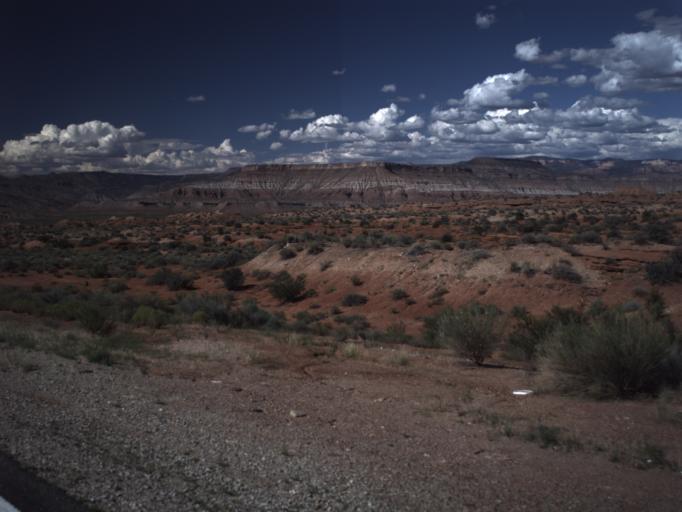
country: US
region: Utah
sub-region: Washington County
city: Hurricane
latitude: 37.1484
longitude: -113.2556
